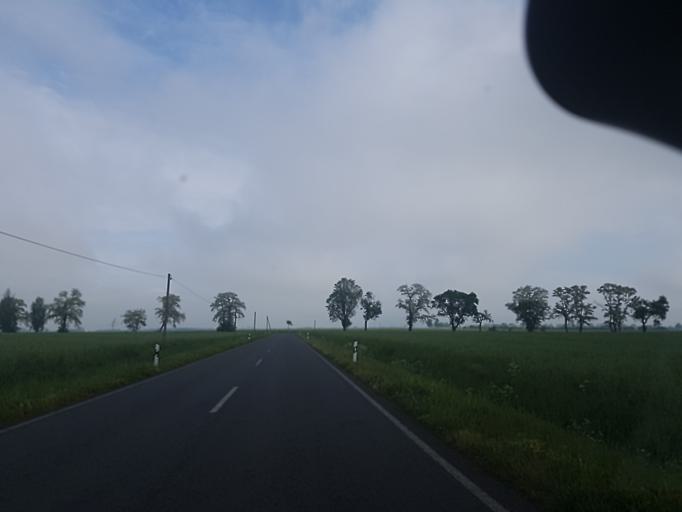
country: DE
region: Saxony-Anhalt
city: Rodleben
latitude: 51.9919
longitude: 12.2319
